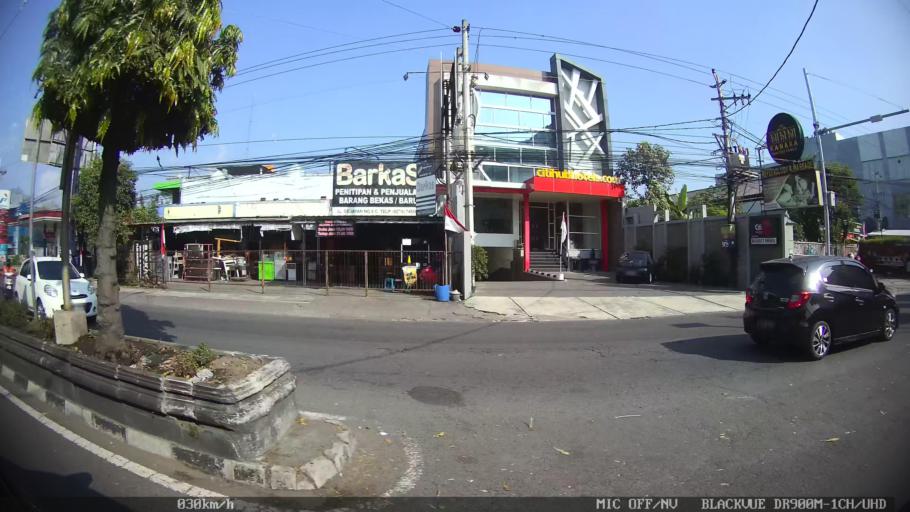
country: ID
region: Daerah Istimewa Yogyakarta
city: Depok
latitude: -7.7599
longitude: 110.3956
